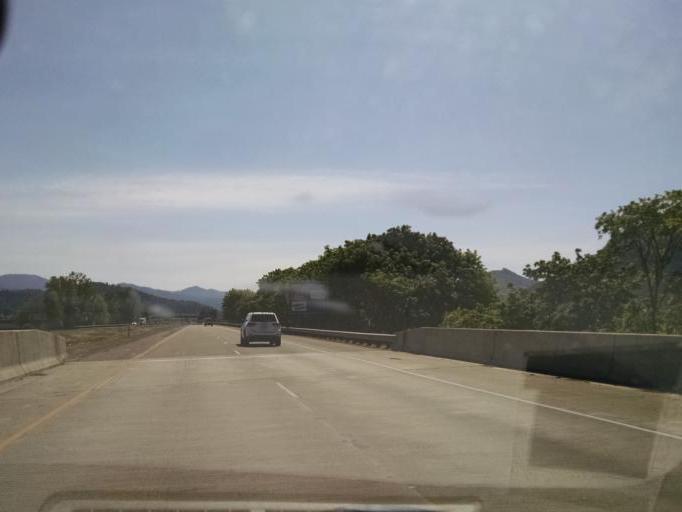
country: US
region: Oregon
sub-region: Douglas County
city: Tri-City
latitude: 42.9925
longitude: -123.3261
